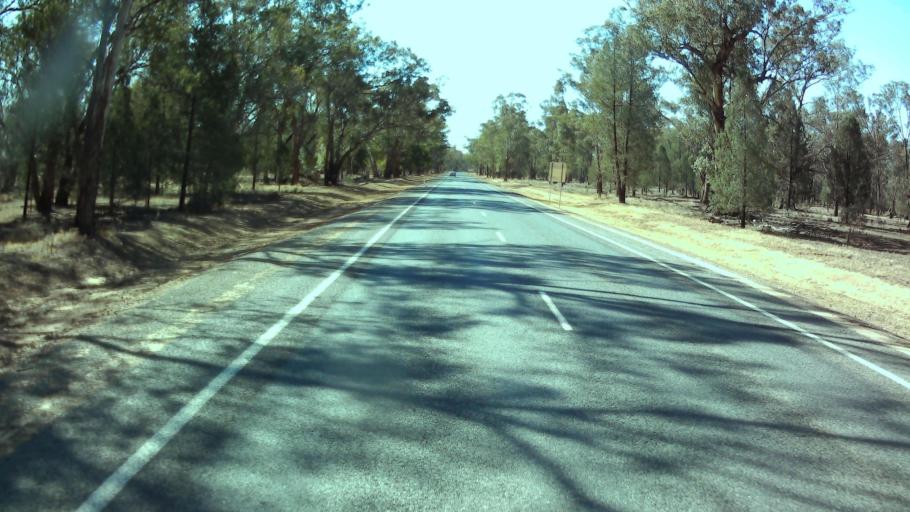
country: AU
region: New South Wales
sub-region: Weddin
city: Grenfell
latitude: -33.7250
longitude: 148.0854
